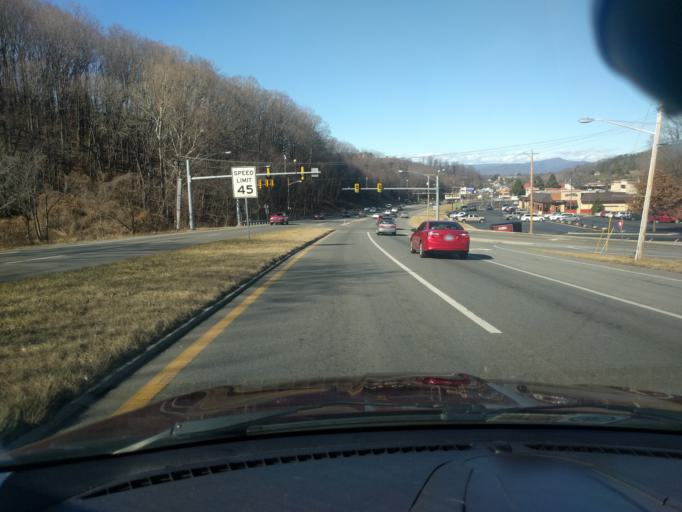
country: US
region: Virginia
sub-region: Roanoke County
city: Narrows
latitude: 37.2194
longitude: -79.9659
